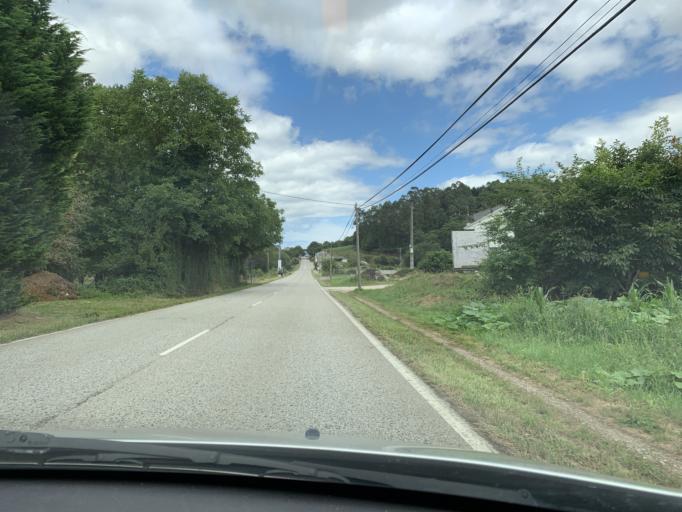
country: ES
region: Galicia
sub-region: Provincia de Lugo
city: Mondonedo
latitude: 43.4401
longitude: -7.3543
